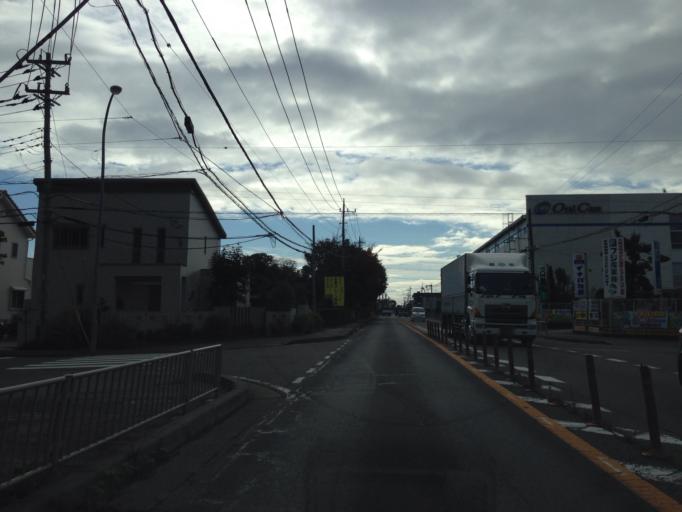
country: JP
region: Ibaraki
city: Ushiku
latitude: 36.0061
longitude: 140.1551
